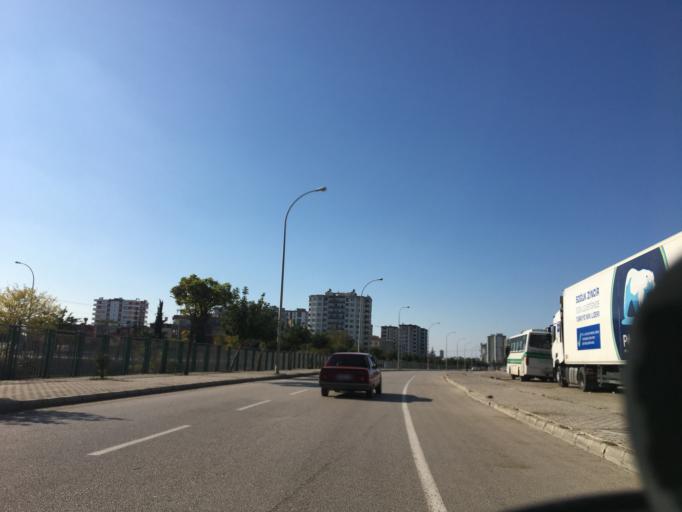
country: TR
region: Adana
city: Seyhan
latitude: 37.0109
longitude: 35.3008
